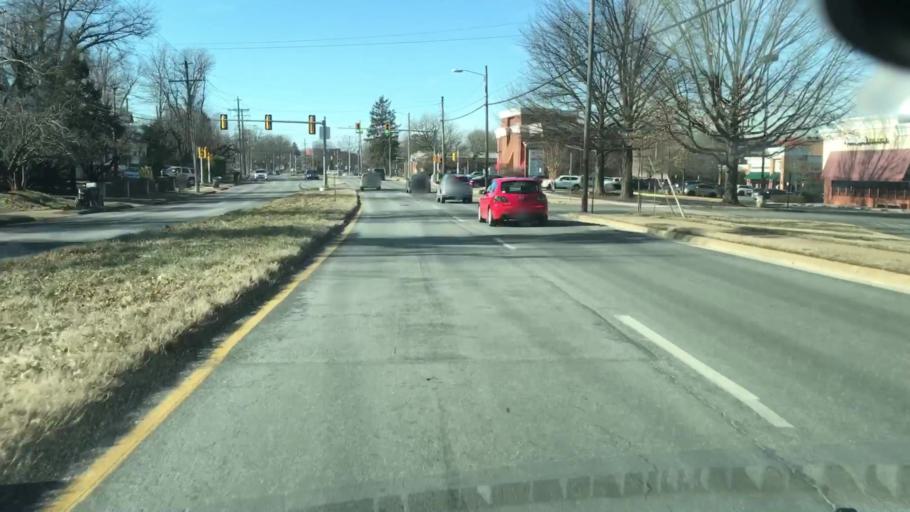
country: US
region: Virginia
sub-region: Fairfax County
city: Oakton
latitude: 38.8823
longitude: -77.2979
